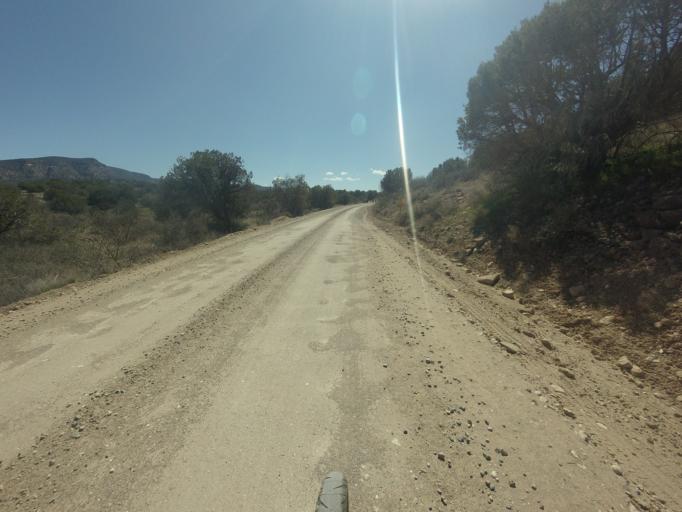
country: US
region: Arizona
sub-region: Yavapai County
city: Lake Montezuma
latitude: 34.6384
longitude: -111.7182
